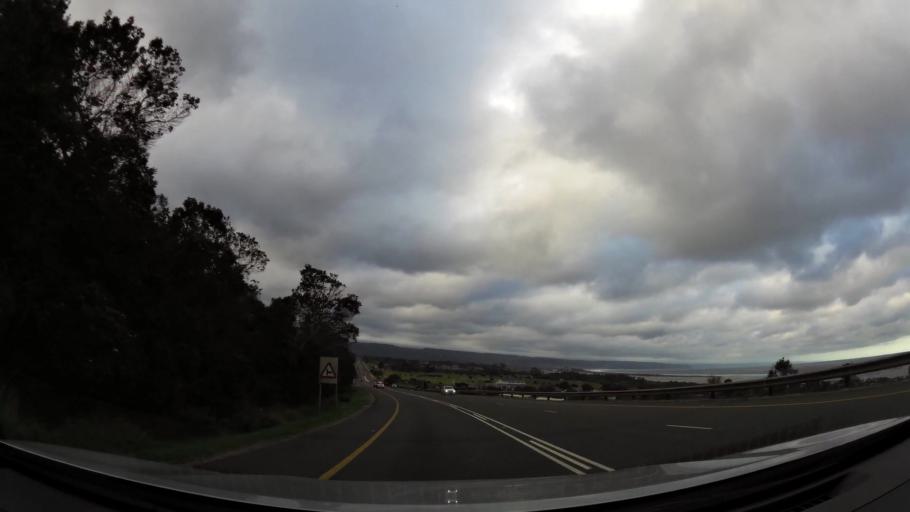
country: ZA
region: Western Cape
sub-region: Eden District Municipality
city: Plettenberg Bay
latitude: -34.0430
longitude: 23.3677
